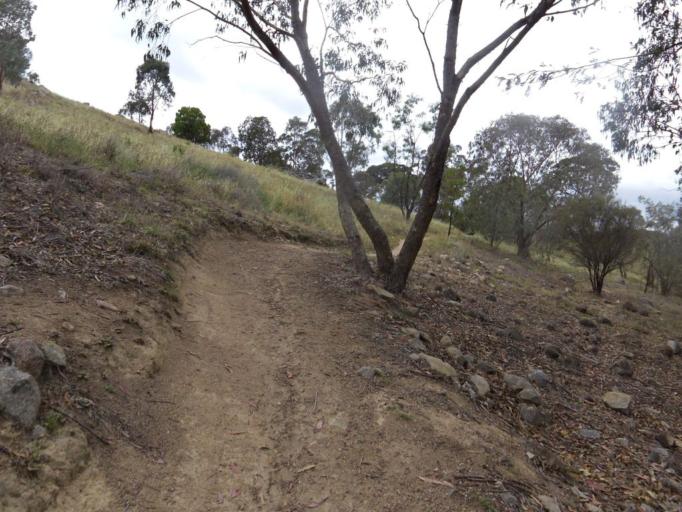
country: AU
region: Australian Capital Territory
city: Forrest
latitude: -35.3577
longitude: 149.0300
